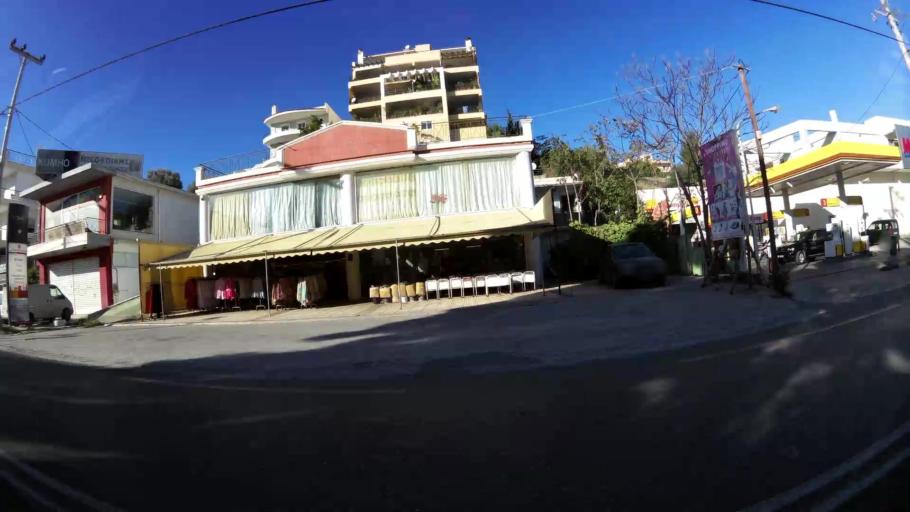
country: GR
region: Attica
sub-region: Nomarchia Anatolikis Attikis
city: Rafina
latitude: 38.0189
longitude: 24.0006
